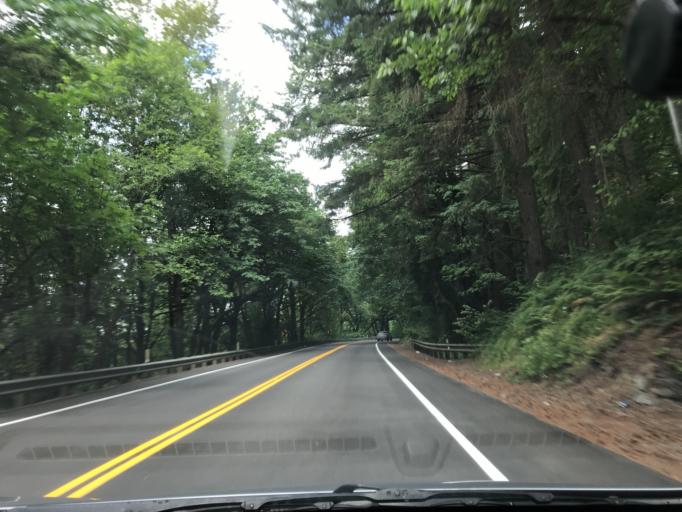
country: US
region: Washington
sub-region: King County
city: Lake Morton-Berrydale
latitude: 47.3172
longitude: -122.1351
